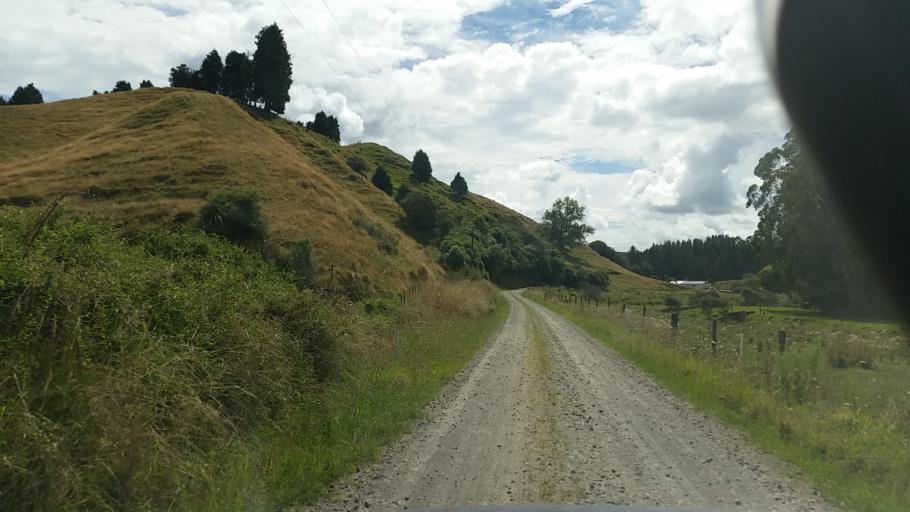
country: NZ
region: Taranaki
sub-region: South Taranaki District
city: Eltham
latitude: -39.2612
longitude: 174.5670
